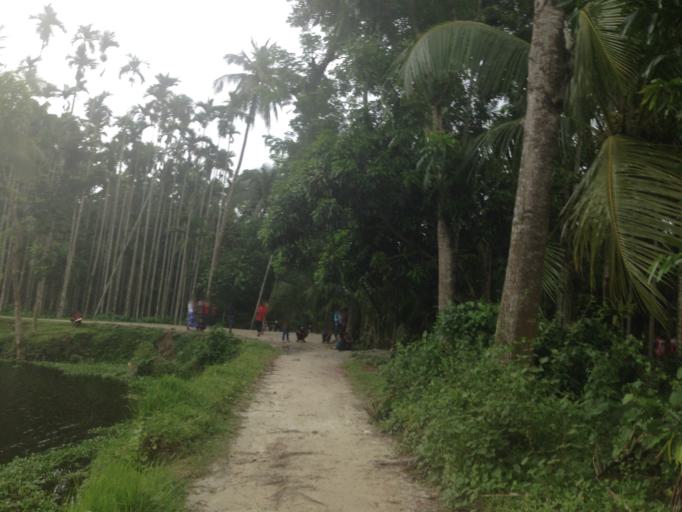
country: BD
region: Chittagong
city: Lakshmipur
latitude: 22.9635
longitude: 90.7954
